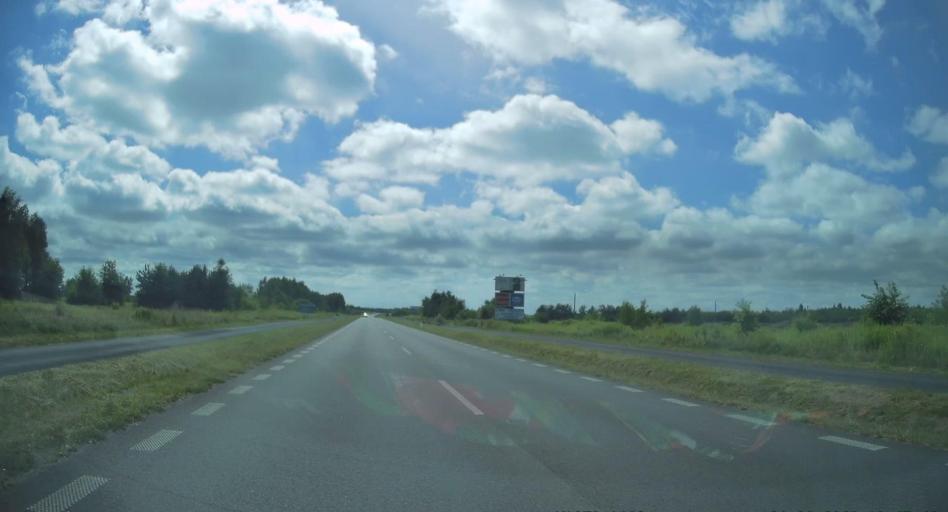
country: PL
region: Subcarpathian Voivodeship
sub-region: Powiat mielecki
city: Padew Narodowa
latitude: 50.3482
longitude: 21.4941
